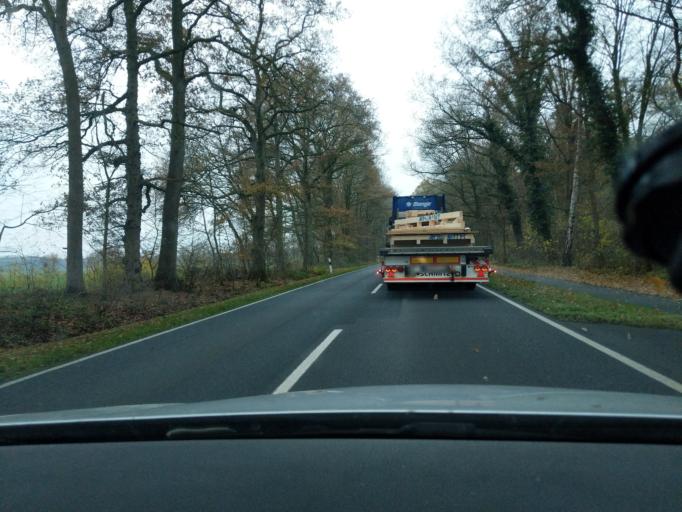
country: DE
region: Lower Saxony
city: Heeslingen
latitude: 53.3034
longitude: 9.3084
